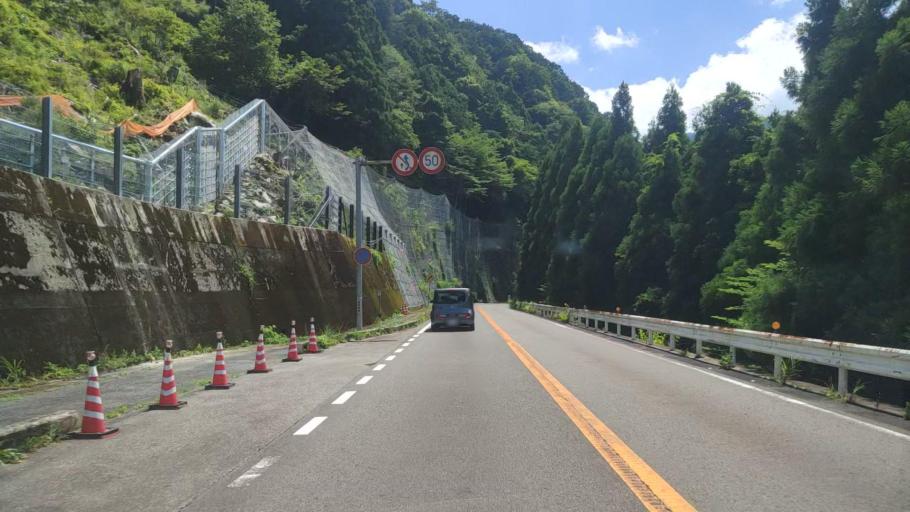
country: JP
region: Mie
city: Owase
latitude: 33.9820
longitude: 136.1072
